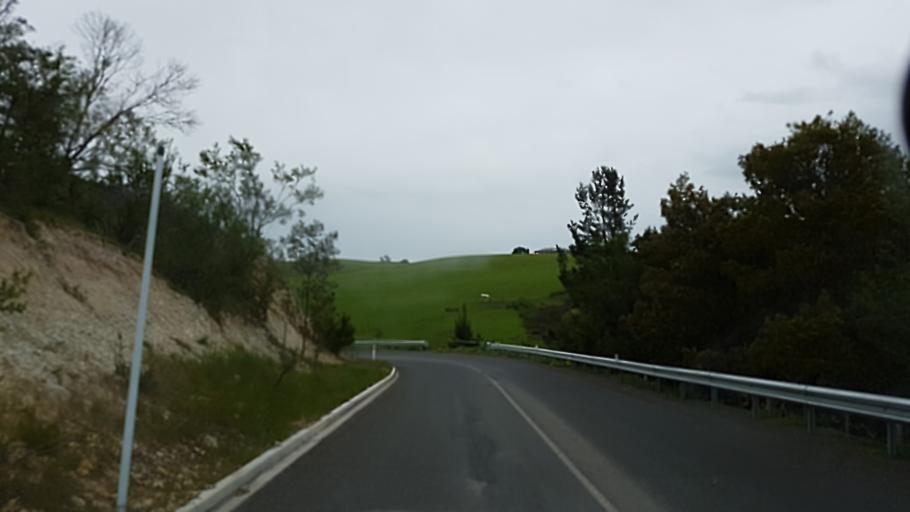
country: AU
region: Victoria
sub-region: Ballarat North
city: Mount Clear
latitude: -37.7850
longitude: 144.1041
